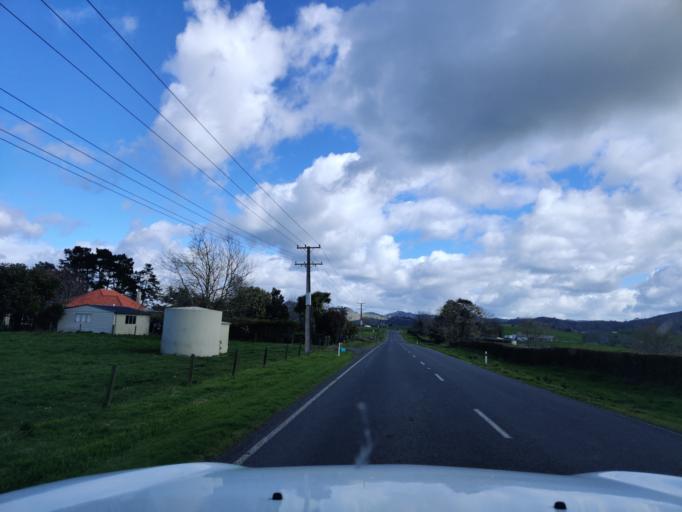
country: NZ
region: Waikato
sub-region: Waikato District
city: Ngaruawahia
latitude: -37.5725
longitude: 175.2483
